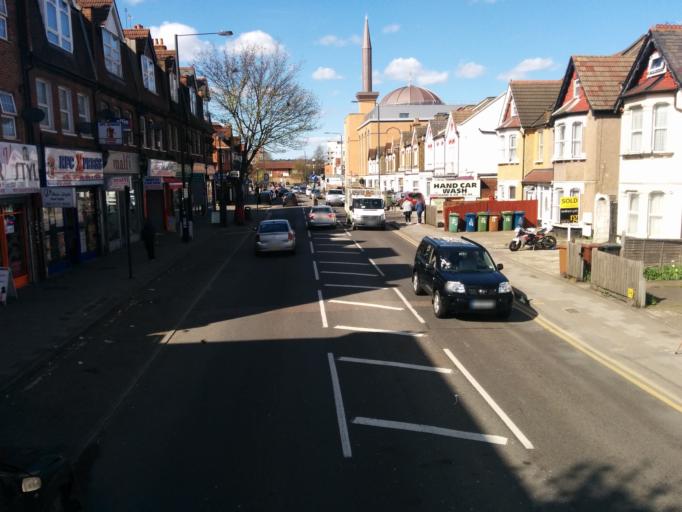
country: GB
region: England
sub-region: Greater London
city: Greenhill
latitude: 51.5878
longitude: -0.3323
